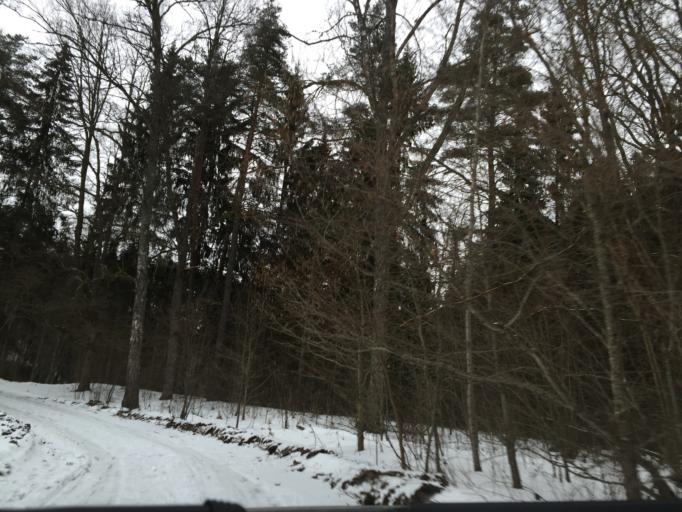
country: LV
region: Seja
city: Loja
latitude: 57.1452
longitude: 24.6816
